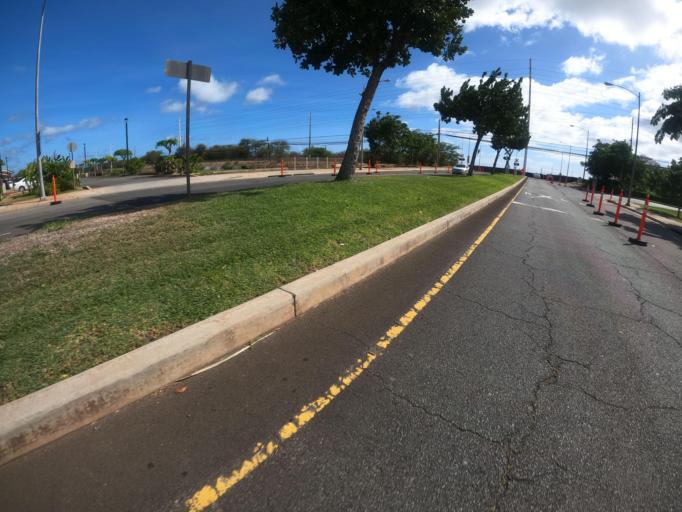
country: US
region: Hawaii
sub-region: Honolulu County
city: Makakilo City
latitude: 21.3268
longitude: -158.0865
